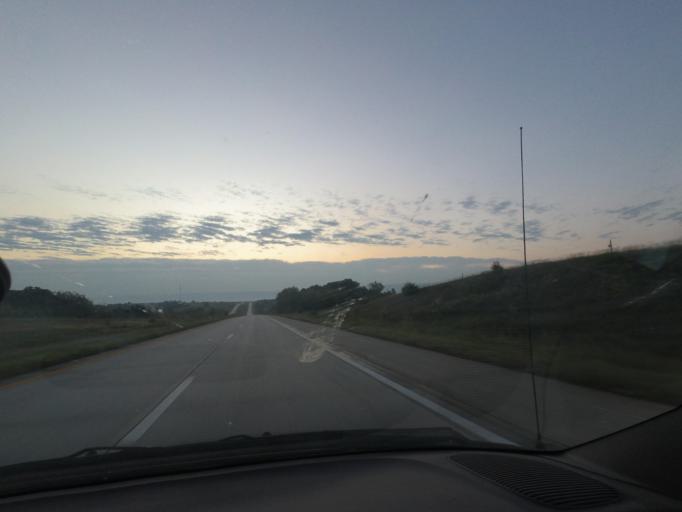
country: US
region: Missouri
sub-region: Linn County
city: Marceline
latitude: 39.7648
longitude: -92.7696
